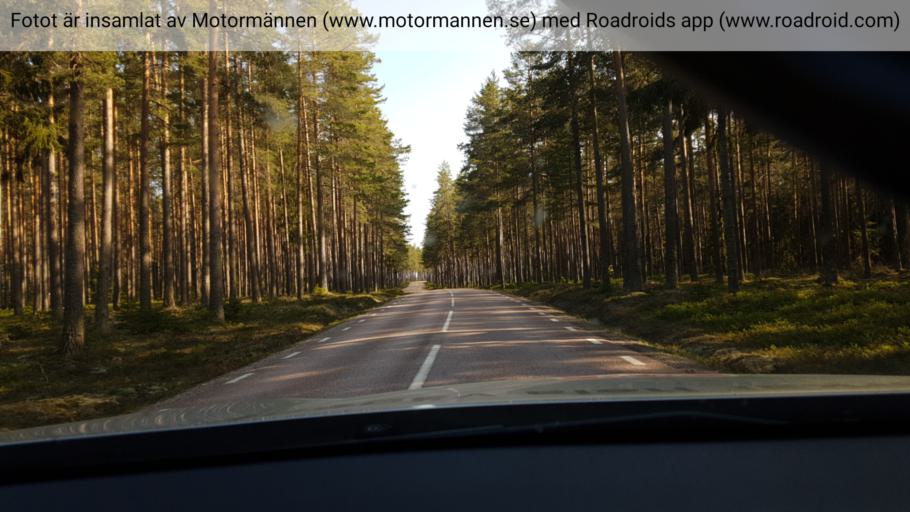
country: SE
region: Gaevleborg
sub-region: Sandvikens Kommun
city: Arsunda
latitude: 60.4302
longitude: 16.6921
